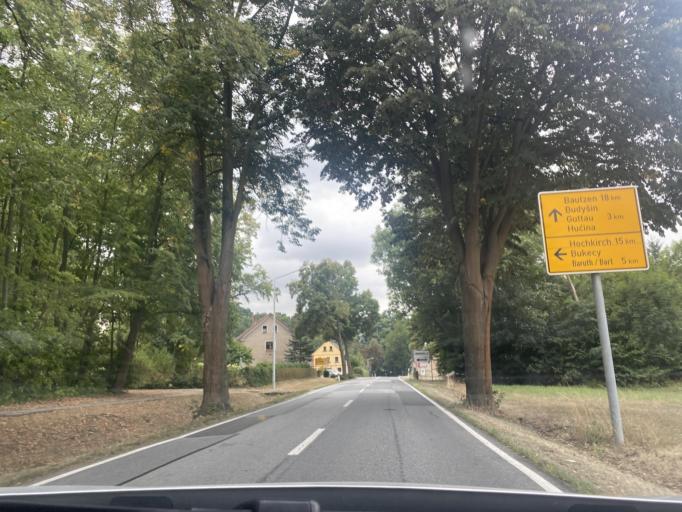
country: DE
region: Saxony
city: Guttau
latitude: 51.2663
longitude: 14.6054
